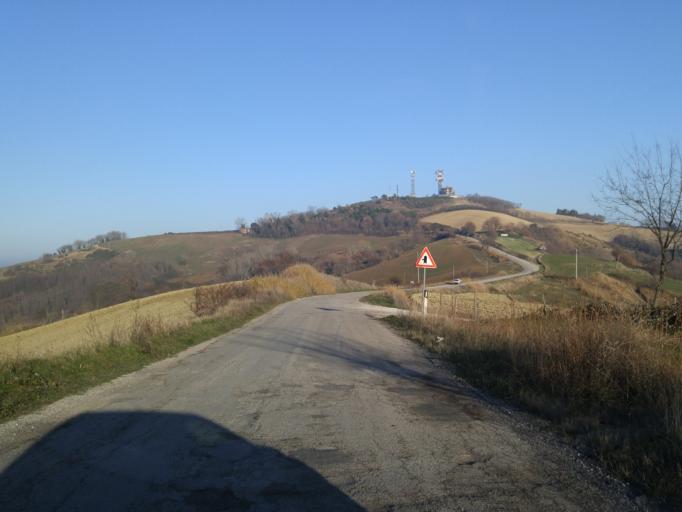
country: IT
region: The Marches
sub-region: Provincia di Pesaro e Urbino
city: Mombaroccio
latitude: 43.7799
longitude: 12.8414
